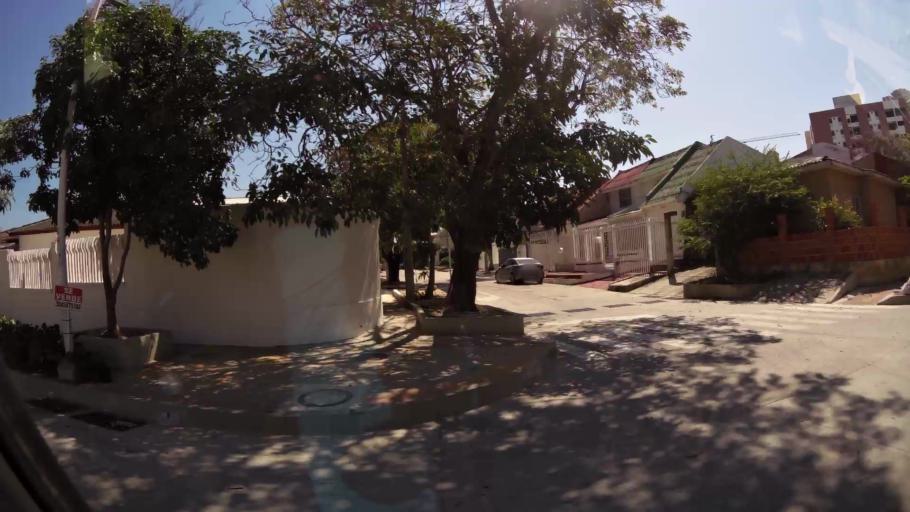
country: CO
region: Atlantico
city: Barranquilla
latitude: 11.0134
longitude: -74.8098
